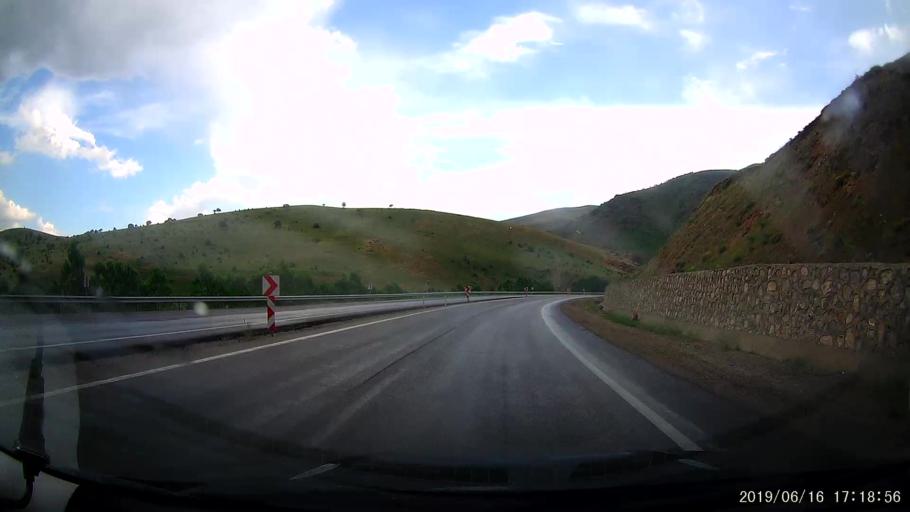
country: TR
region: Erzincan
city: Tercan
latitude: 39.8066
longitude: 40.5310
